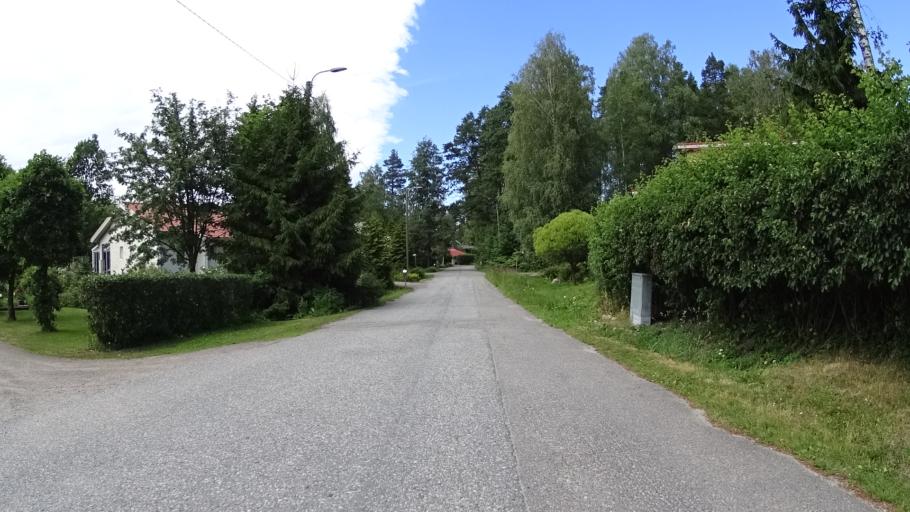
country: FI
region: Uusimaa
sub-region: Helsinki
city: Kilo
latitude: 60.3218
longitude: 24.8348
